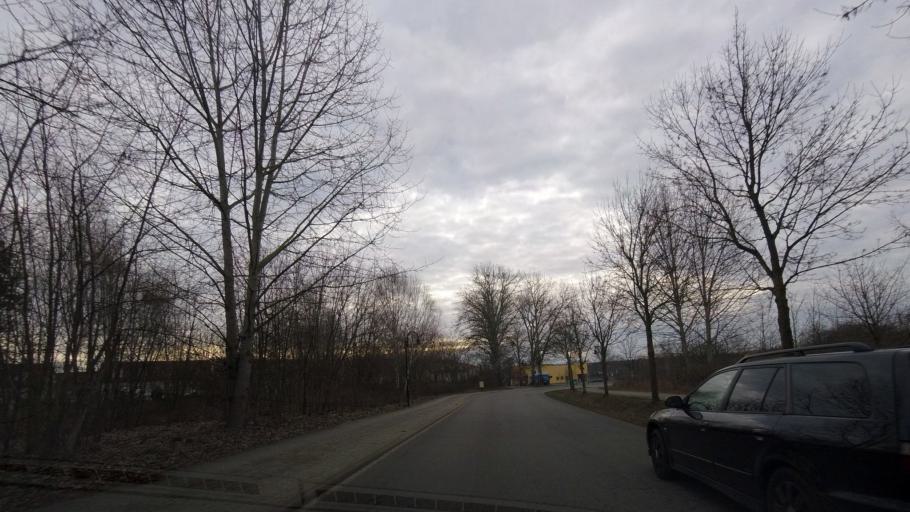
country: DE
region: Brandenburg
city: Woltersdorf
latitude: 52.4561
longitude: 13.7372
